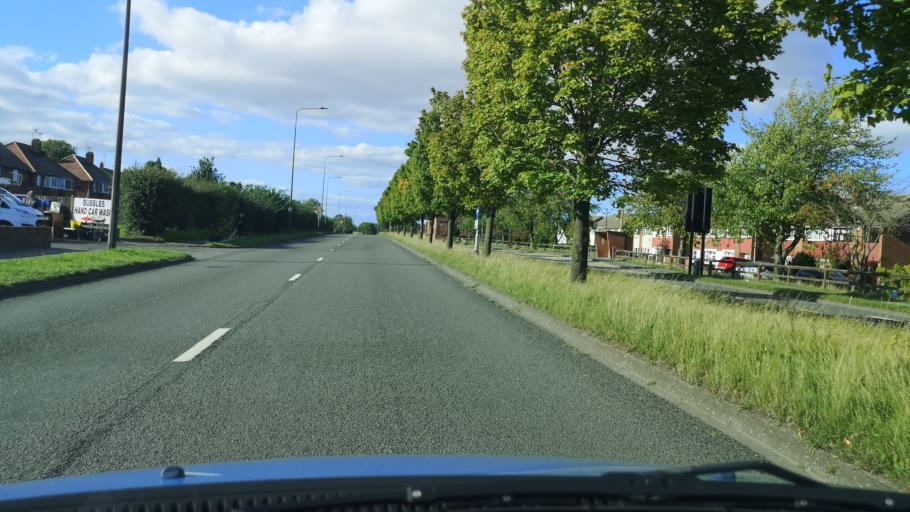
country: GB
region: England
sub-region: Doncaster
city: Carcroft
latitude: 53.5687
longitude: -1.1988
